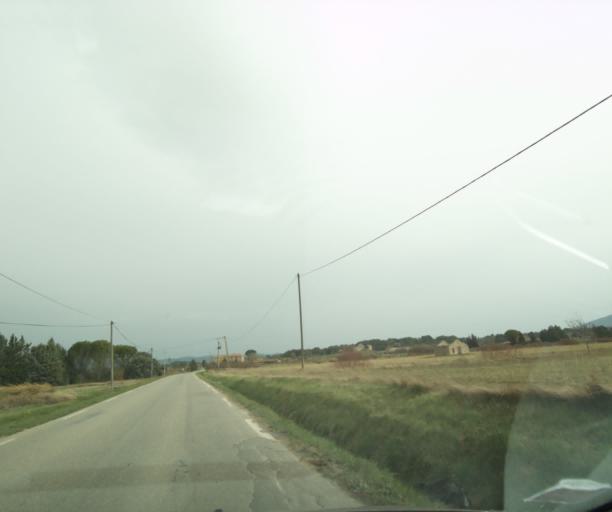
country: FR
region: Provence-Alpes-Cote d'Azur
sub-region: Departement des Bouches-du-Rhone
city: Trets
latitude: 43.4643
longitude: 5.7030
